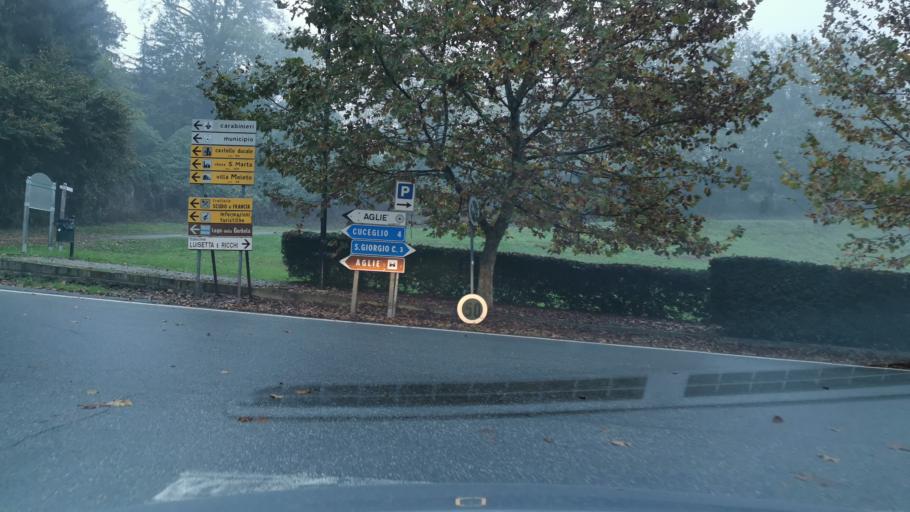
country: IT
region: Piedmont
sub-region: Provincia di Torino
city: Aglie
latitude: 45.3603
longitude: 7.7720
